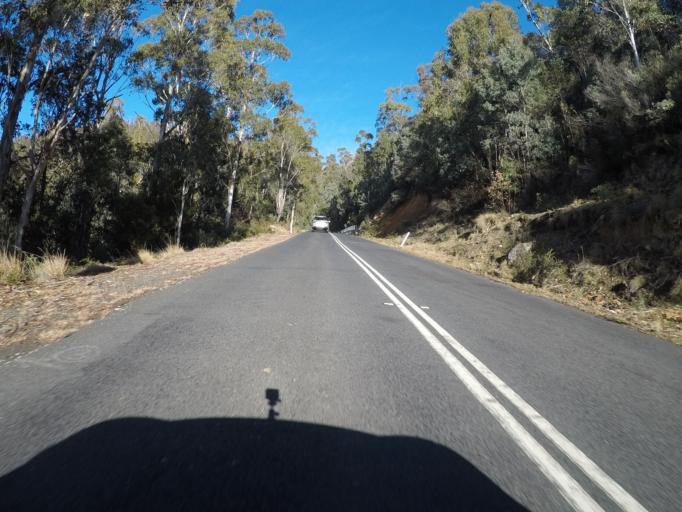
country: AU
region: Australian Capital Territory
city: Macarthur
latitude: -35.4860
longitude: 148.9327
